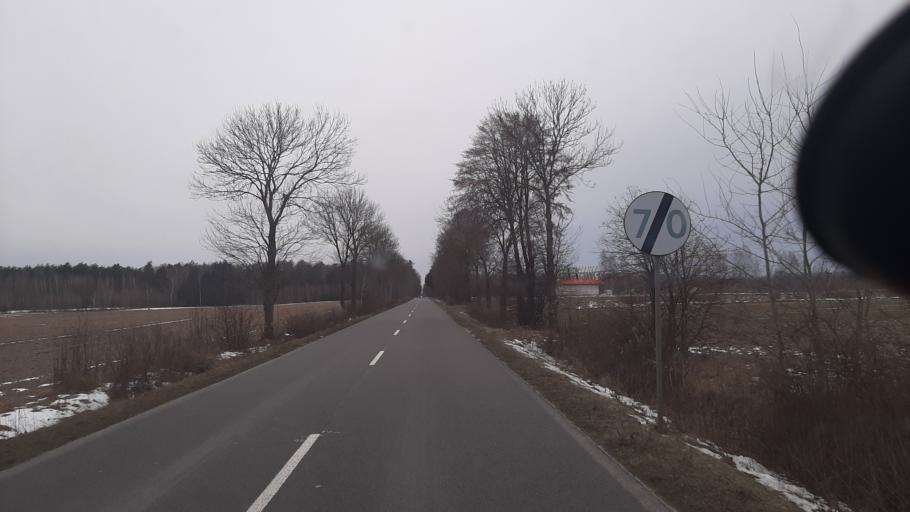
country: PL
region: Lublin Voivodeship
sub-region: Powiat lubartowski
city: Kamionka
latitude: 51.4954
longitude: 22.4200
